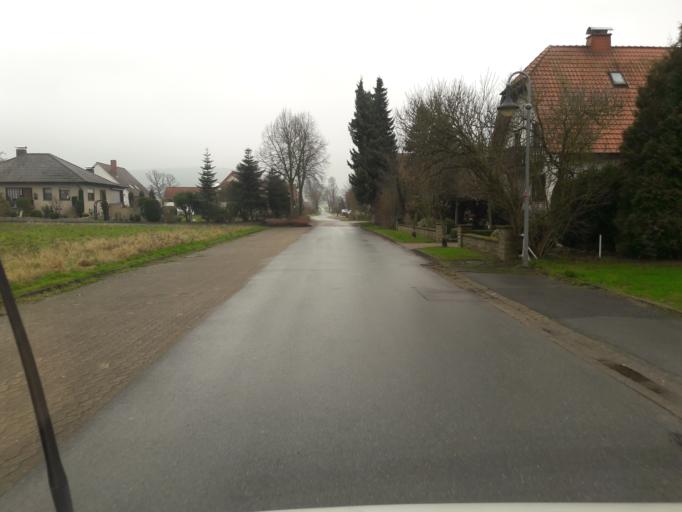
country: DE
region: North Rhine-Westphalia
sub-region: Regierungsbezirk Detmold
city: Hille
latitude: 52.2953
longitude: 8.7684
